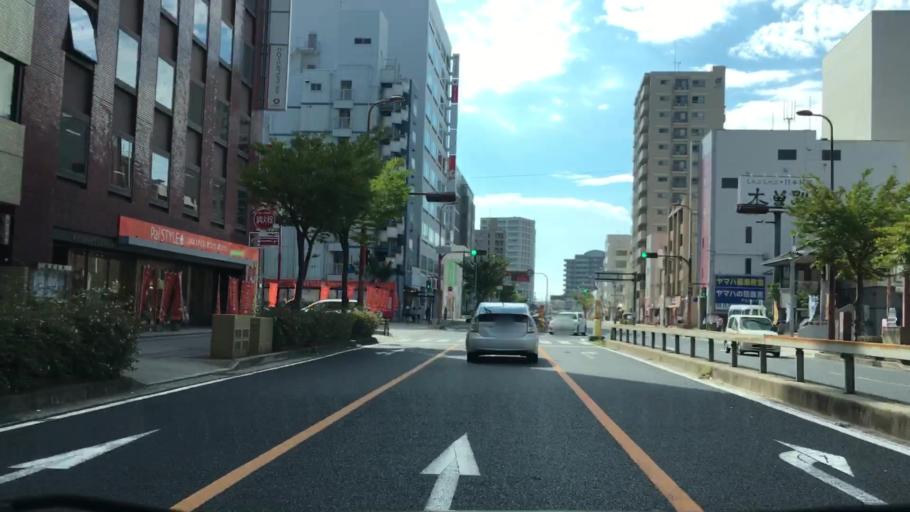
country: JP
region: Hyogo
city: Akashi
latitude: 34.6479
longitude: 134.9889
